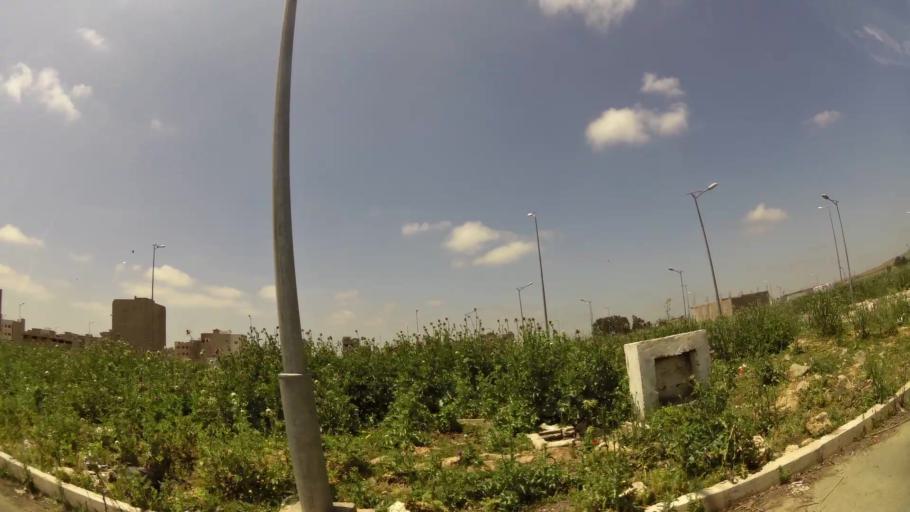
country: MA
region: Fes-Boulemane
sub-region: Fes
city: Fes
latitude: 34.0379
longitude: -5.0540
